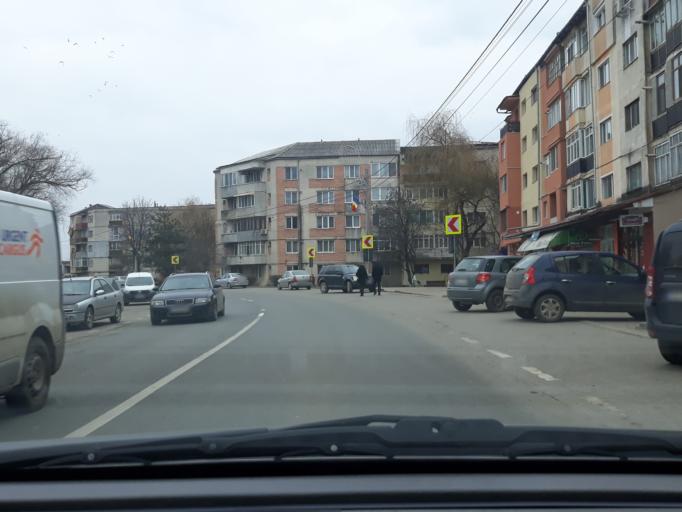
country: RO
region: Salaj
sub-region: Oras Simleu Silvaniei
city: Simleu Silvaniei
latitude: 47.2265
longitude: 22.7930
